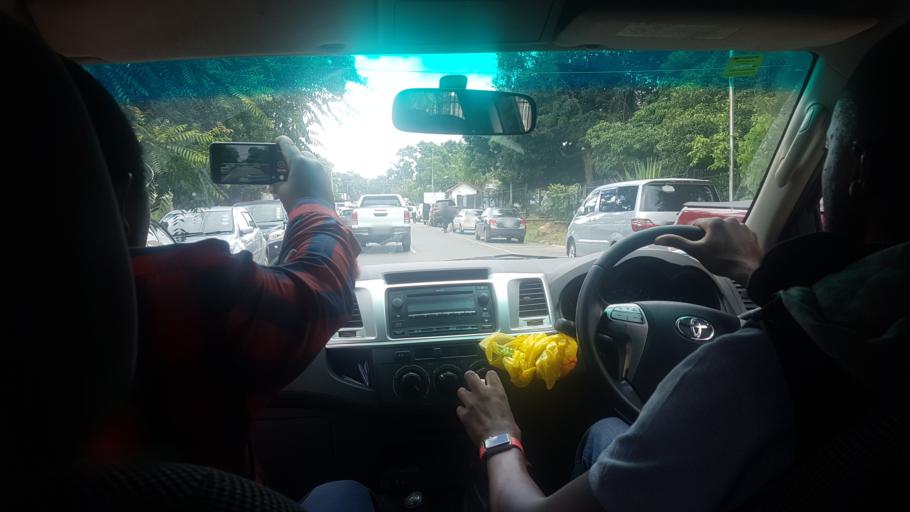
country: ZM
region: Lusaka
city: Lusaka
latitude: -15.4251
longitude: 28.3087
